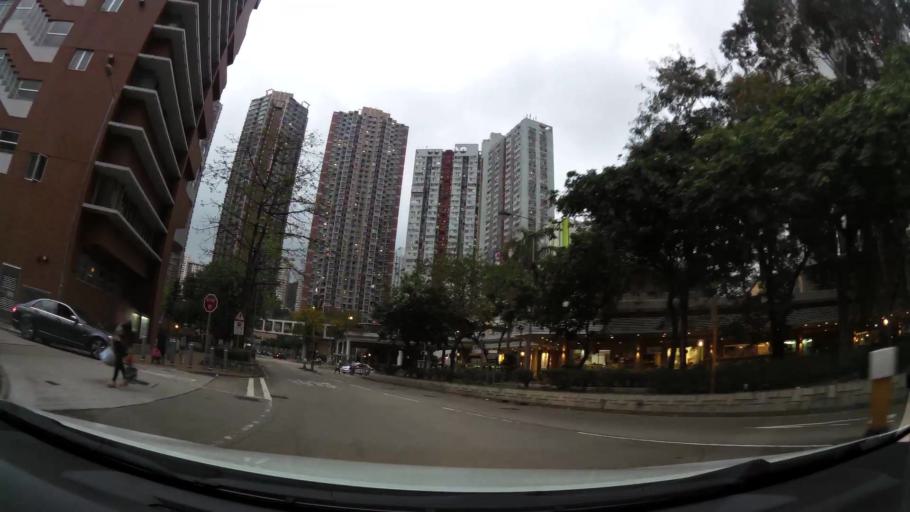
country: HK
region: Tsuen Wan
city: Tsuen Wan
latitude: 22.3549
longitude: 114.1040
